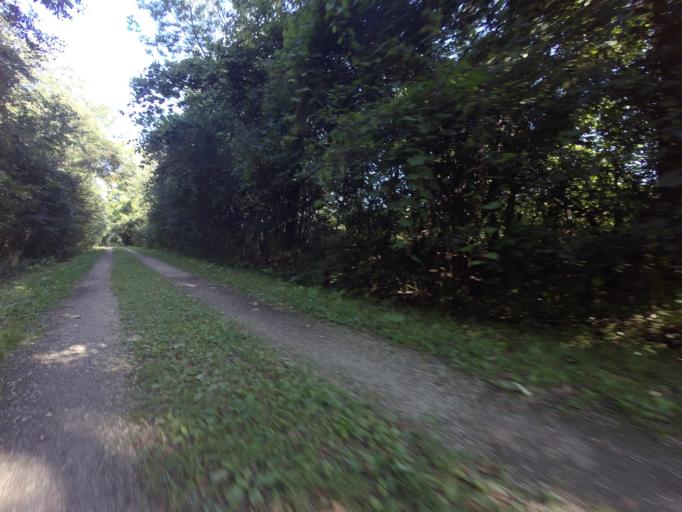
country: CA
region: Ontario
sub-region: Wellington County
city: Guelph
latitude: 43.6540
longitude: -80.4204
